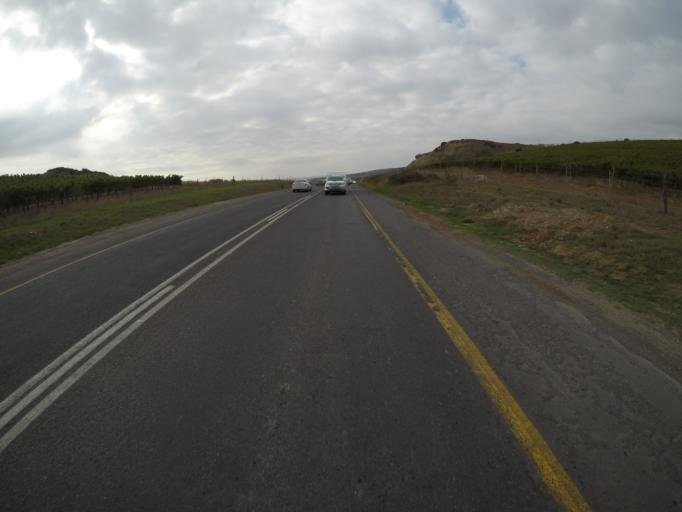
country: ZA
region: Western Cape
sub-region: City of Cape Town
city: Sunset Beach
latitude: -33.8334
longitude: 18.5903
